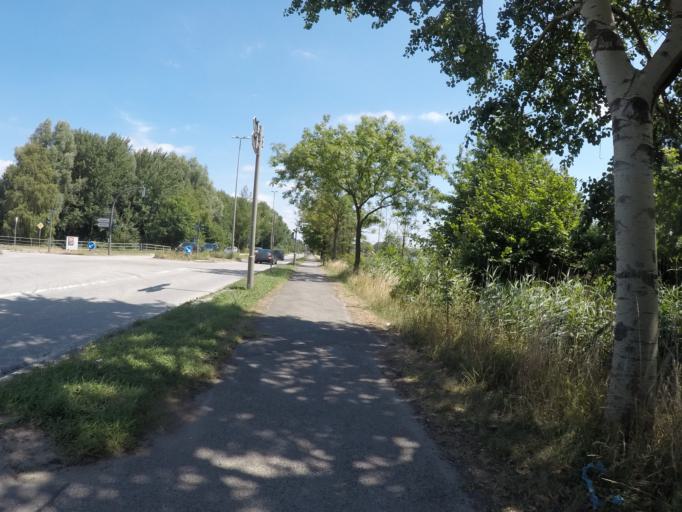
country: DE
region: Hamburg
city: Harburg
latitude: 53.4805
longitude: 10.0086
